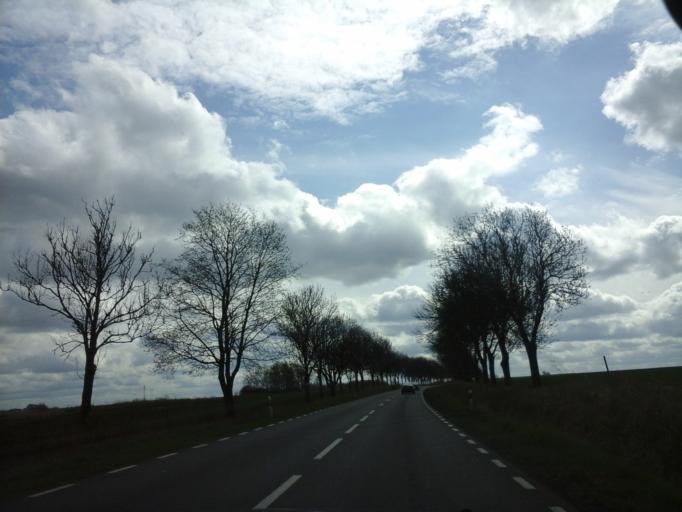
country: PL
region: West Pomeranian Voivodeship
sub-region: Powiat choszczenski
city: Pelczyce
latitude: 53.0597
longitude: 15.3017
